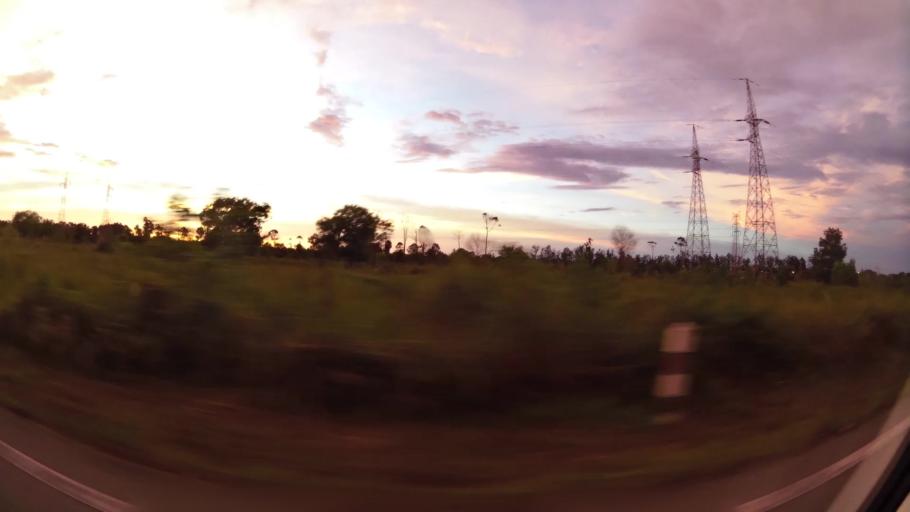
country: BN
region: Belait
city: Seria
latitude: 4.6304
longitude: 114.3868
